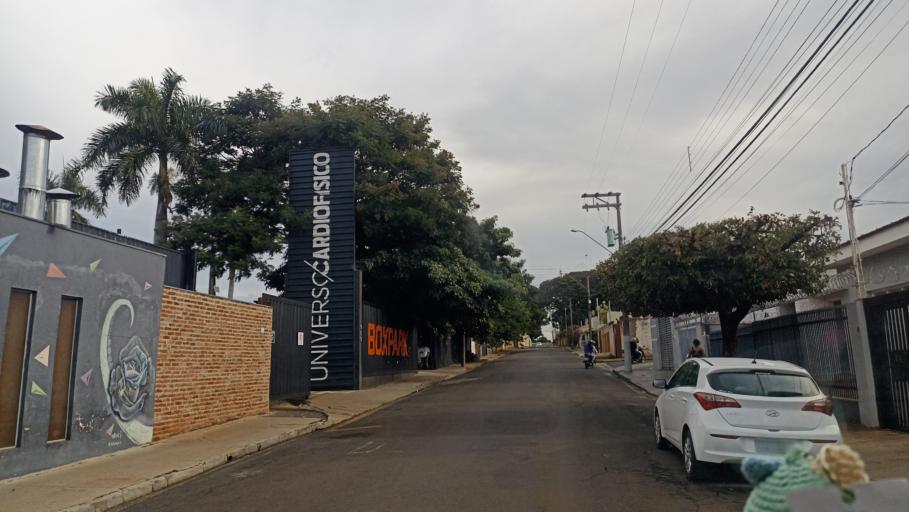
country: BR
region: Sao Paulo
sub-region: Jaboticabal
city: Jaboticabal
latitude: -21.2592
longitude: -48.3257
